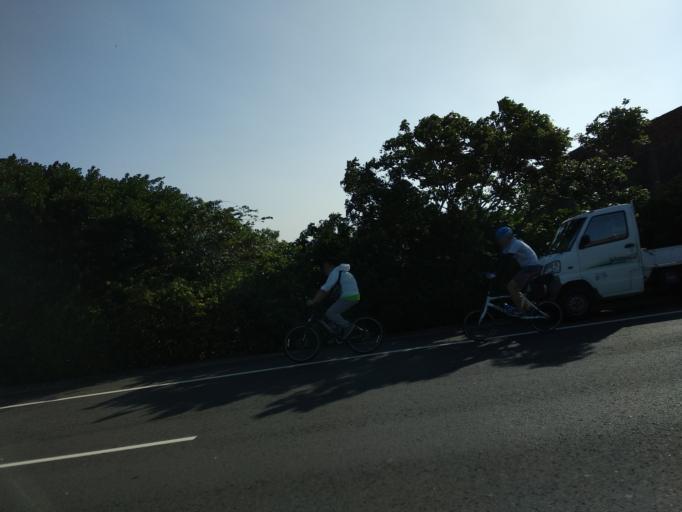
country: TW
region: Taiwan
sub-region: Hsinchu
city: Zhubei
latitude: 24.9859
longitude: 121.0505
